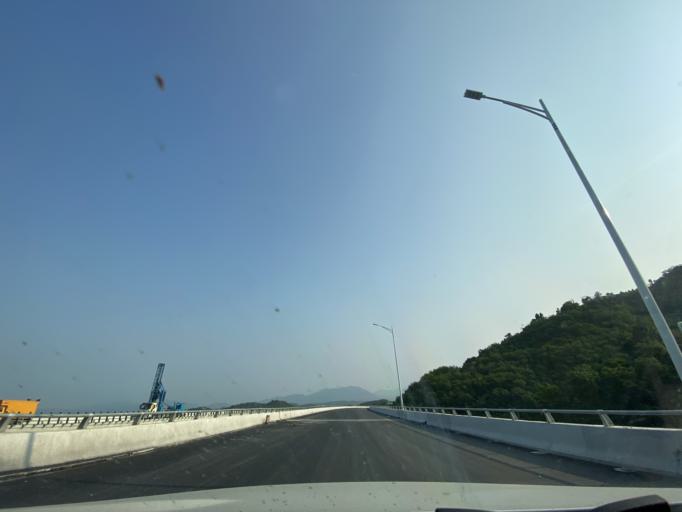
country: CN
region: Hainan
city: Xiangshui
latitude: 18.6615
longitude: 109.6287
